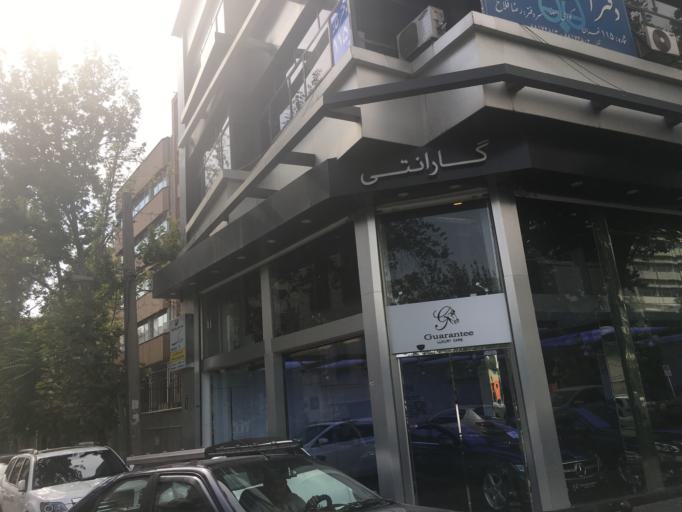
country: IR
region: Tehran
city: Tehran
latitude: 35.7349
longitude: 51.4455
